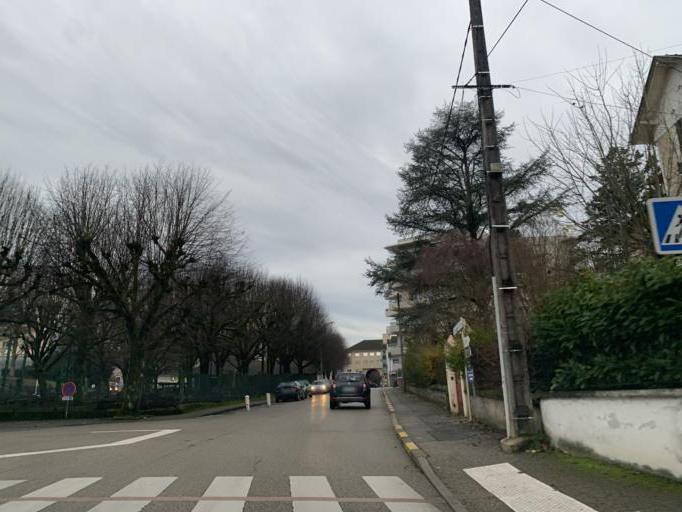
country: FR
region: Rhone-Alpes
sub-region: Departement de l'Ain
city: Belley
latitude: 45.7605
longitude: 5.6920
